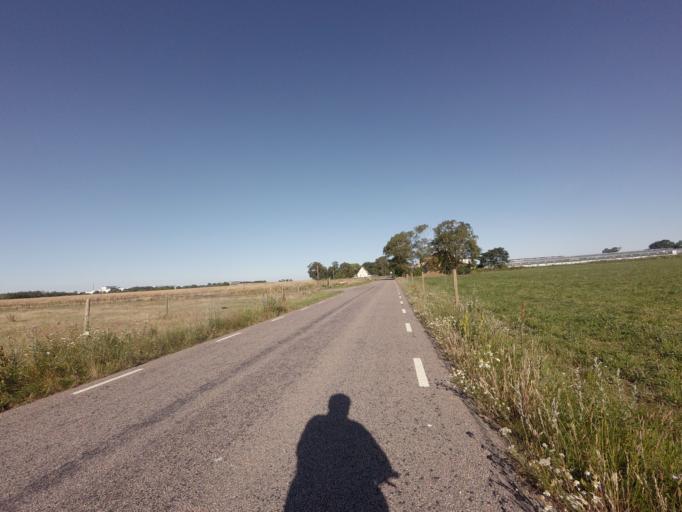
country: SE
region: Skane
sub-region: Hoganas Kommun
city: Hoganas
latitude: 56.1649
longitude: 12.5966
